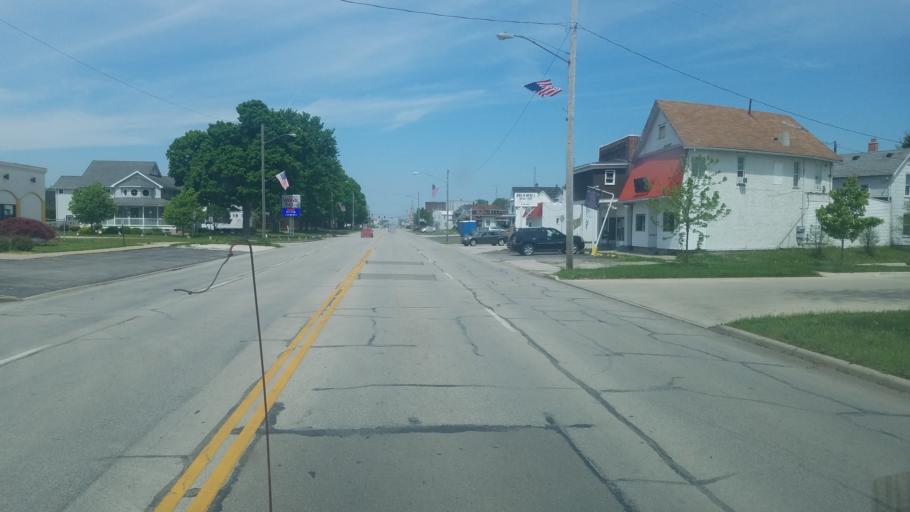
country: US
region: Ohio
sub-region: Sandusky County
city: Fremont
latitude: 41.3533
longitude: -83.1280
